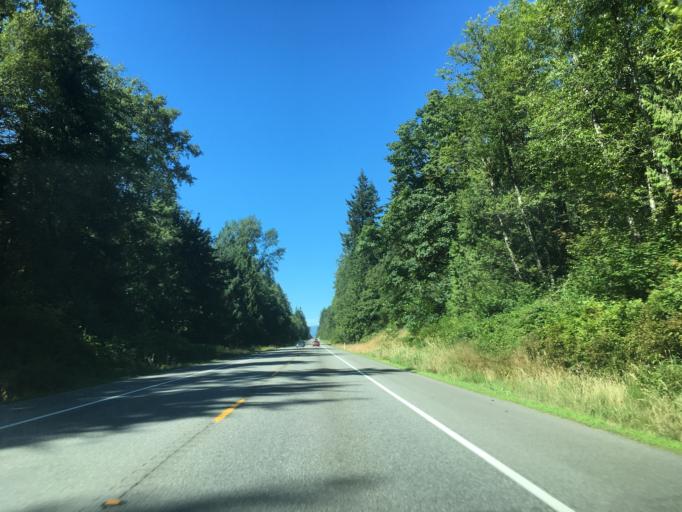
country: US
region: Washington
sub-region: Snohomish County
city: Sisco Heights
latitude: 48.1038
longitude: -122.1121
